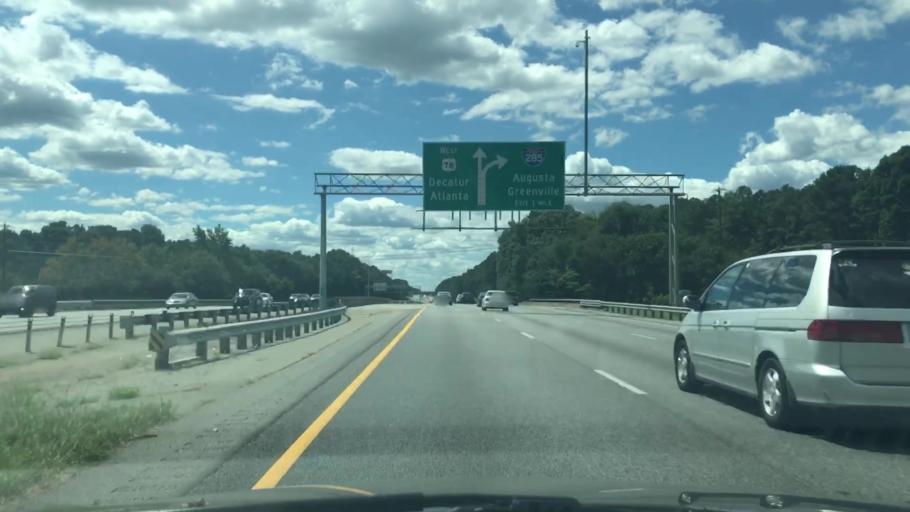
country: US
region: Georgia
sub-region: DeKalb County
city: Clarkston
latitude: 33.8257
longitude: -84.2327
